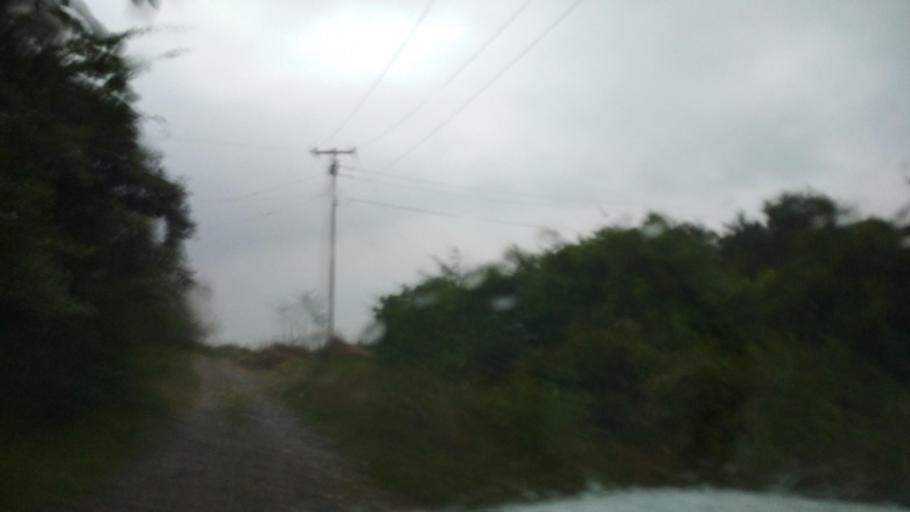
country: MM
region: Shan
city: Taunggyi
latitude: 20.2999
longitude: 97.3027
